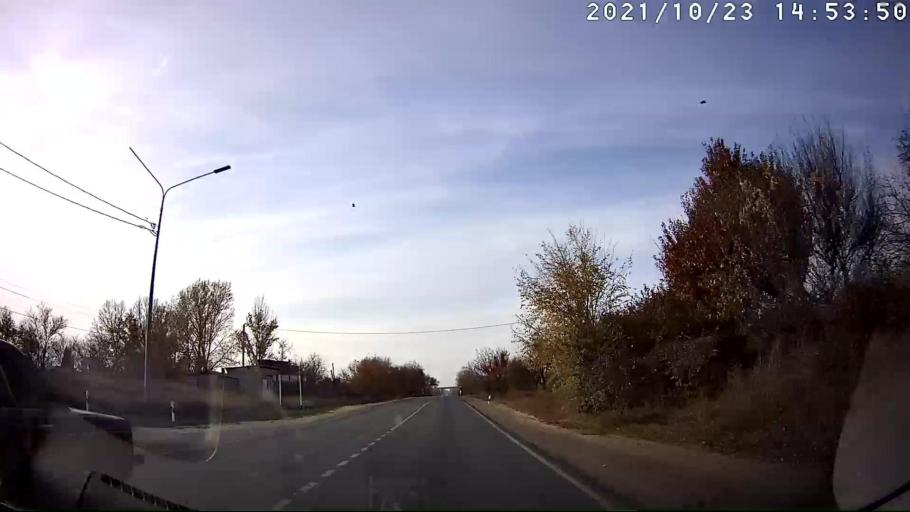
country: RU
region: Volgograd
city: Volgograd
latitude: 48.4436
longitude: 44.4254
